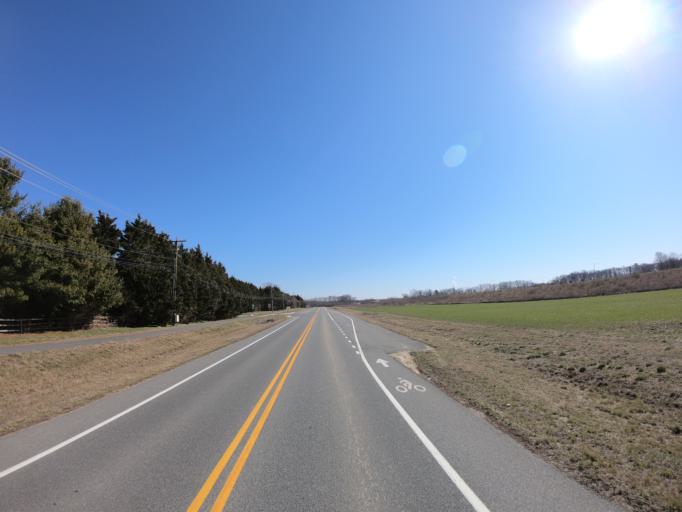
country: US
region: Delaware
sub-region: New Castle County
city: Middletown
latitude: 39.5262
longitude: -75.6745
